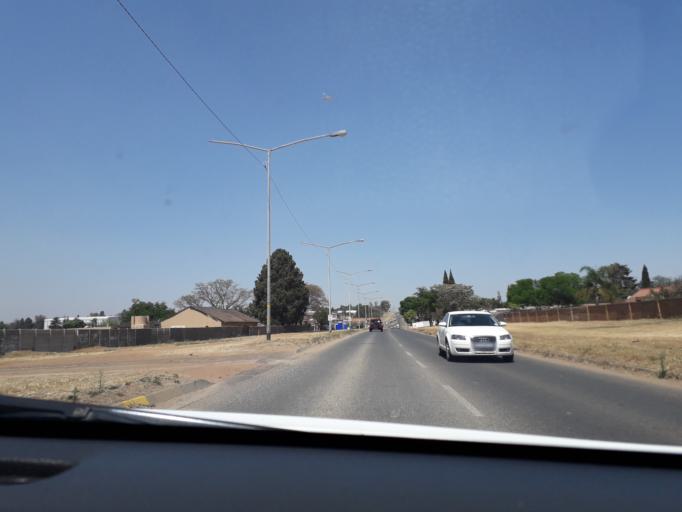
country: ZA
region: Gauteng
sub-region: City of Johannesburg Metropolitan Municipality
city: Modderfontein
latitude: -26.0836
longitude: 28.2489
